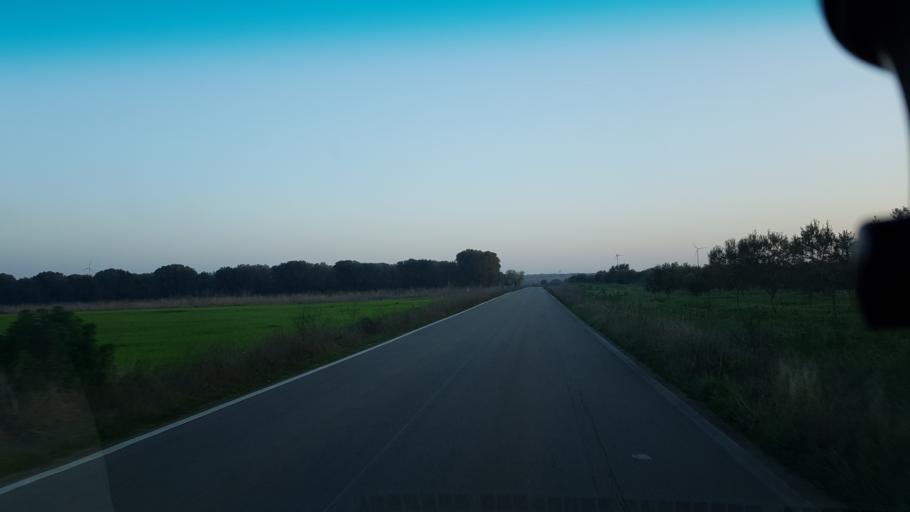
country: IT
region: Apulia
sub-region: Provincia di Brindisi
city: Mesagne
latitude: 40.6248
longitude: 17.7835
